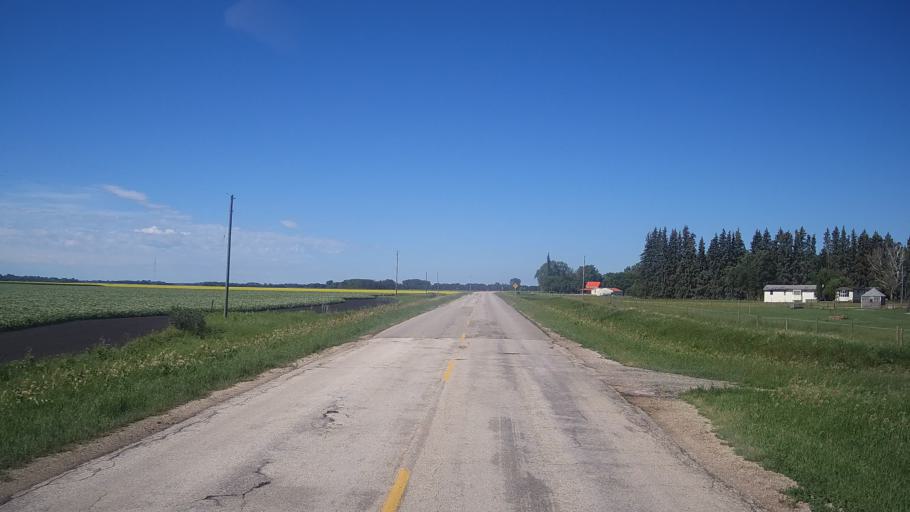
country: CA
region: Manitoba
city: Portage la Prairie
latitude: 50.0360
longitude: -98.0785
